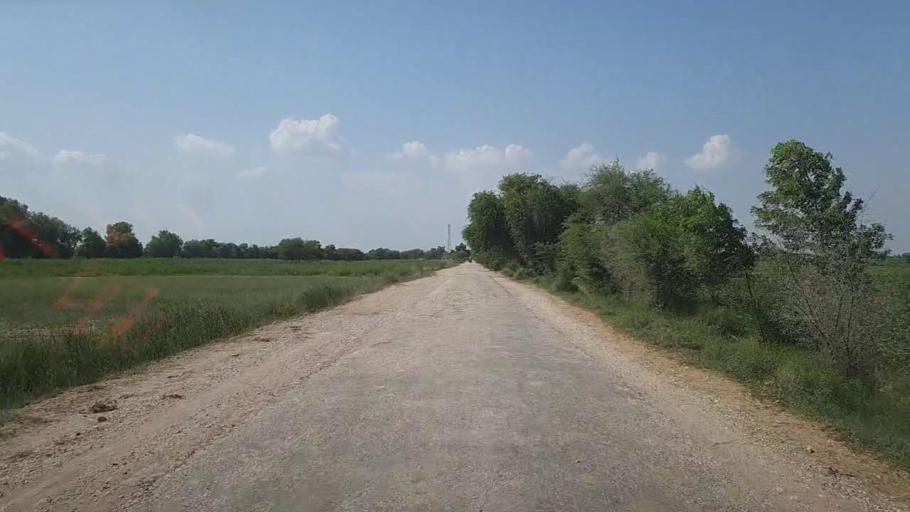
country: PK
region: Sindh
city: Khairpur
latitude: 28.1134
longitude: 69.6191
